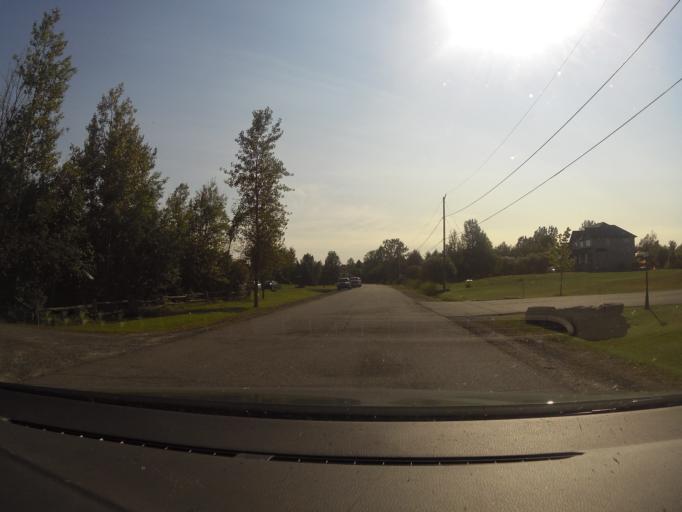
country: CA
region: Ontario
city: Carleton Place
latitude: 45.2927
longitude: -76.0674
